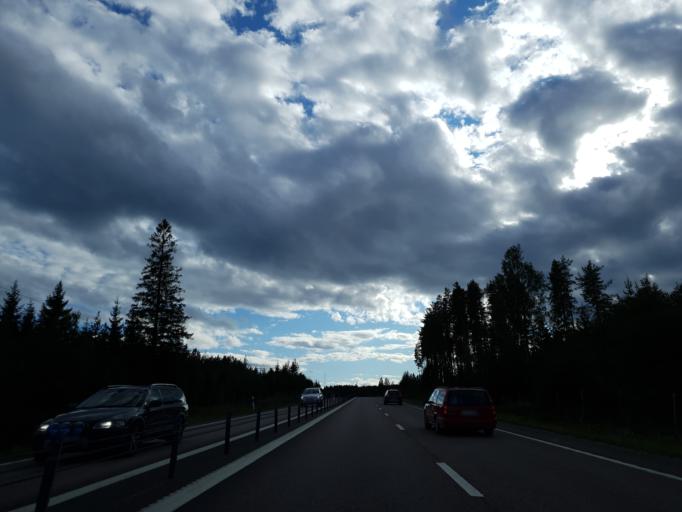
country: SE
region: Vaesternorrland
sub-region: Haernoesands Kommun
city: Haernoesand
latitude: 62.5782
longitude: 17.7577
